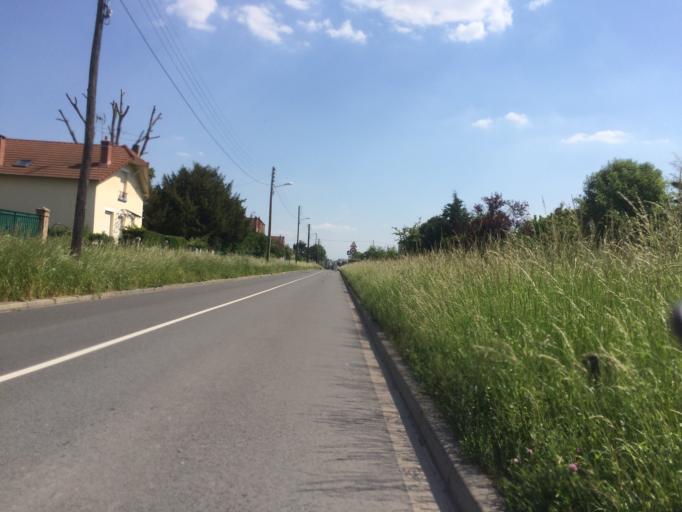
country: FR
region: Ile-de-France
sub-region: Departement de l'Essonne
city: Savigny-sur-Orge
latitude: 48.6870
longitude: 2.3583
